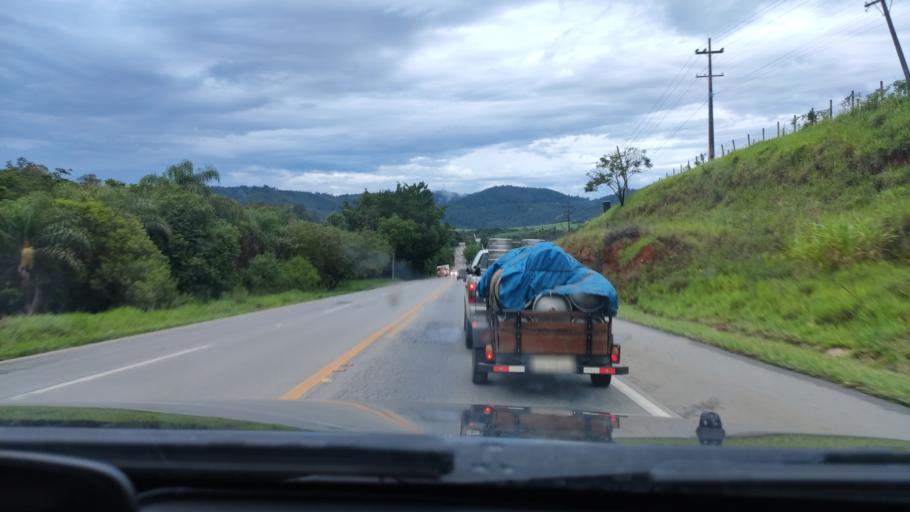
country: BR
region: Sao Paulo
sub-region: Braganca Paulista
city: Braganca Paulista
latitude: -22.8562
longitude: -46.5431
